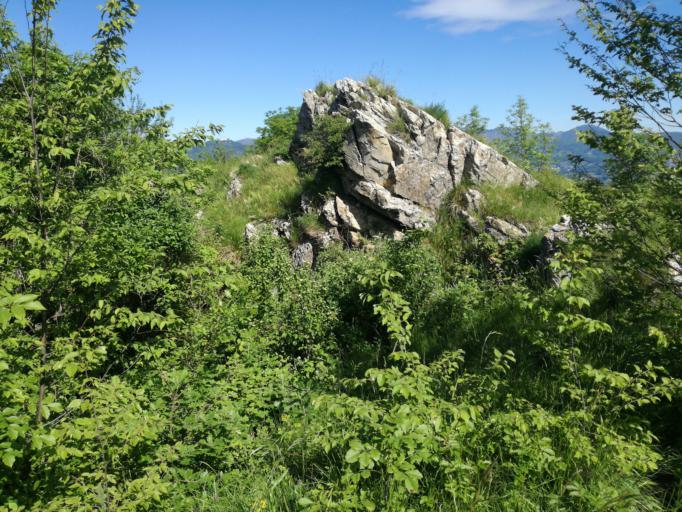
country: IT
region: Liguria
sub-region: Provincia di Genova
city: Manesseno
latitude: 44.4575
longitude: 8.9367
